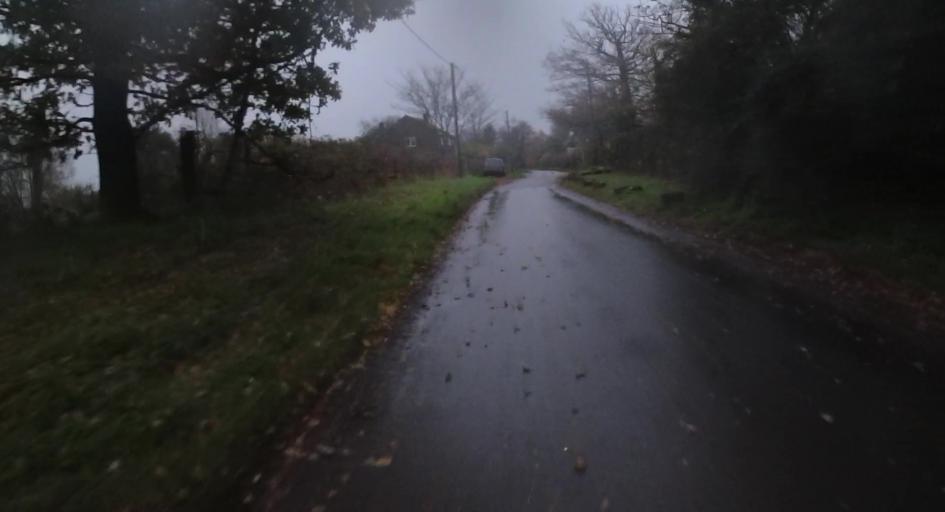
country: GB
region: England
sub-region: Wokingham
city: Swallowfield
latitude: 51.3718
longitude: -0.9527
